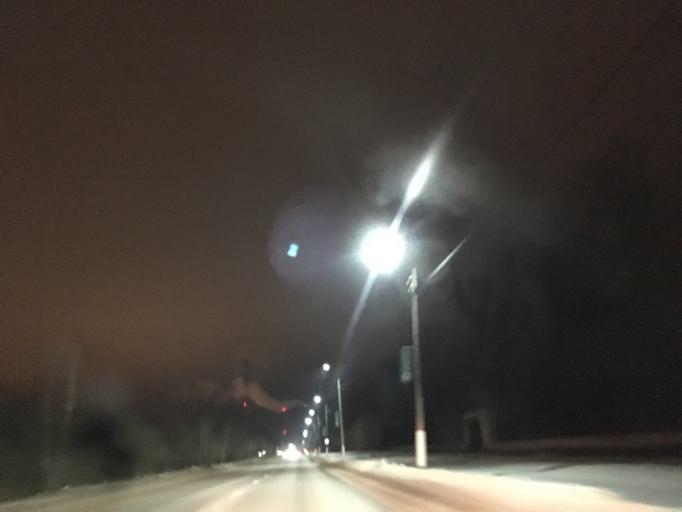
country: RU
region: Tula
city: Pervomayskiy
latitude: 54.0372
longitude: 37.5137
